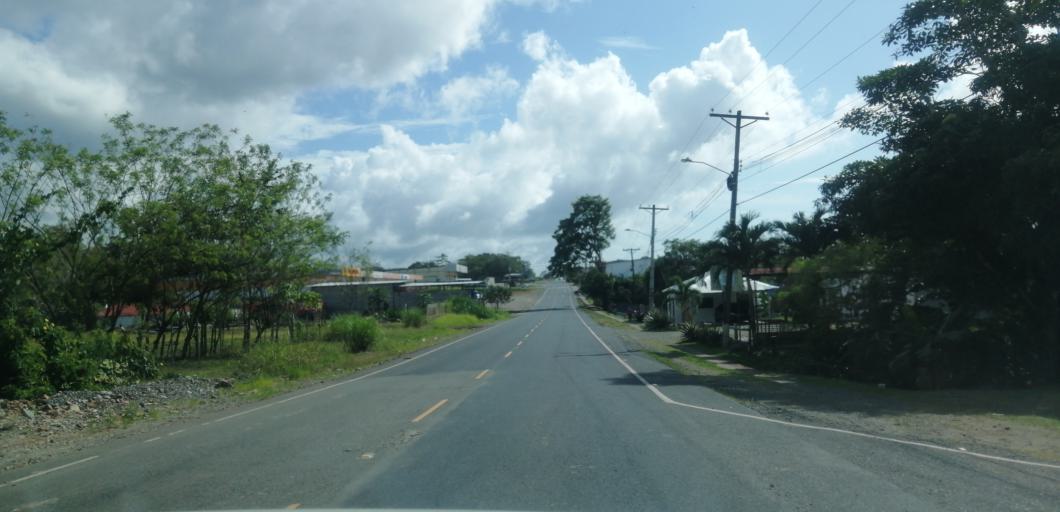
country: PA
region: Panama
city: Canita
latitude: 9.2214
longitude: -78.8955
